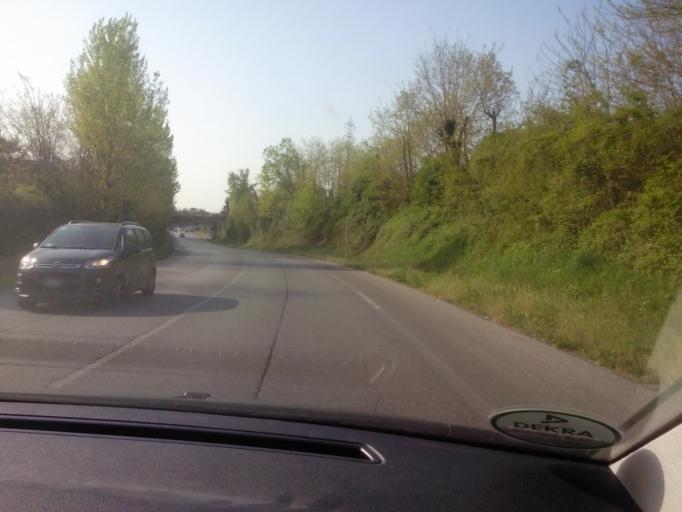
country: IT
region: Lombardy
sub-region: Provincia di Brescia
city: Desenzano del Garda
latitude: 45.4738
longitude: 10.5266
